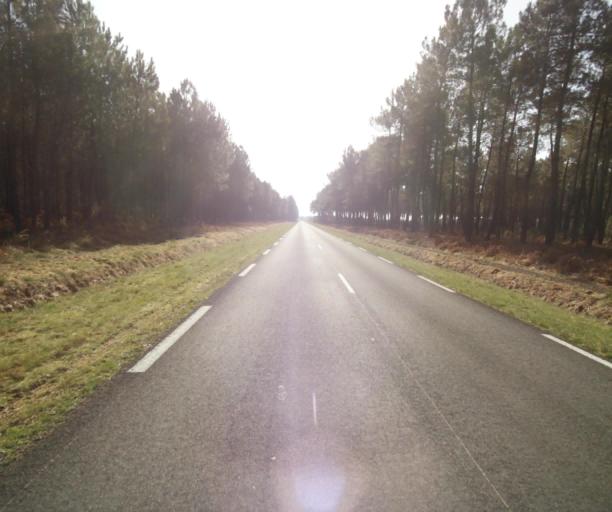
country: FR
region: Aquitaine
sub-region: Departement de la Gironde
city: Grignols
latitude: 44.1810
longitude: -0.1442
